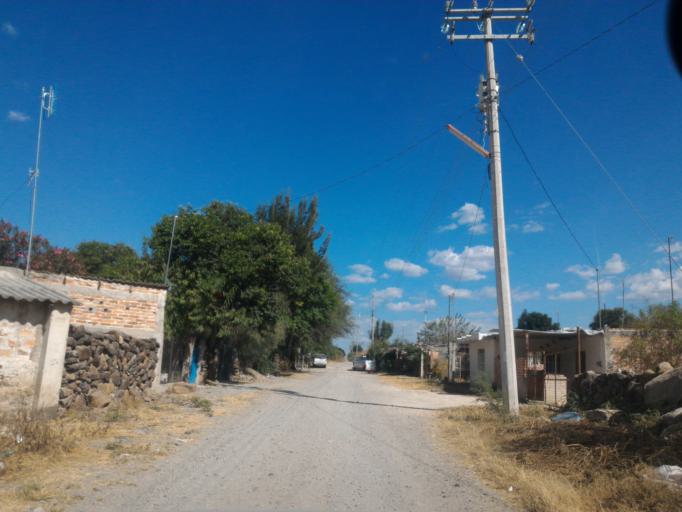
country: MX
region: Jalisco
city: San Diego de Alejandria
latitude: 20.8819
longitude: -102.0115
